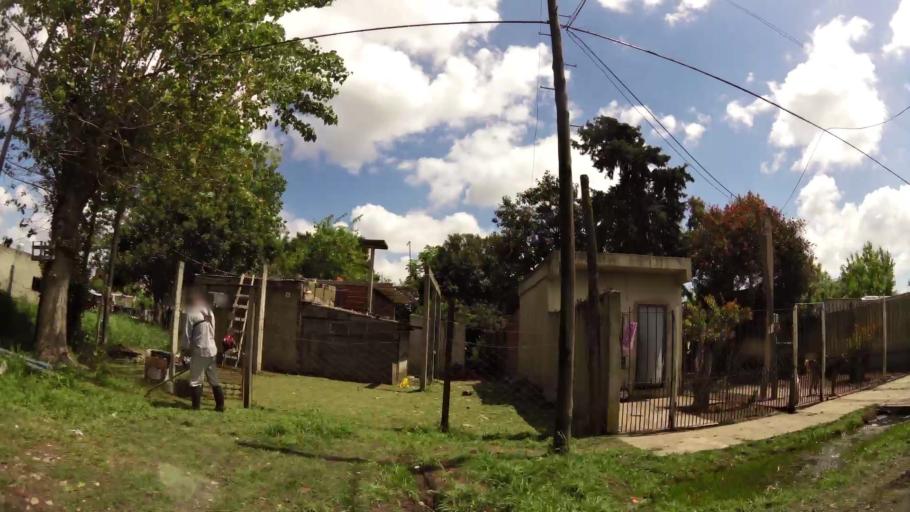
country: AR
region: Buenos Aires
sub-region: Partido de Quilmes
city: Quilmes
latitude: -34.8427
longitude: -58.2319
